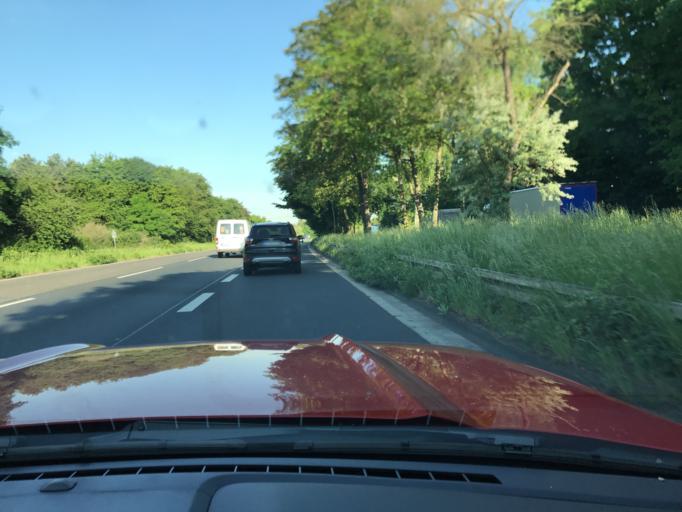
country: DE
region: North Rhine-Westphalia
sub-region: Regierungsbezirk Koln
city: Leverkusen
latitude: 51.0261
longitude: 6.9313
